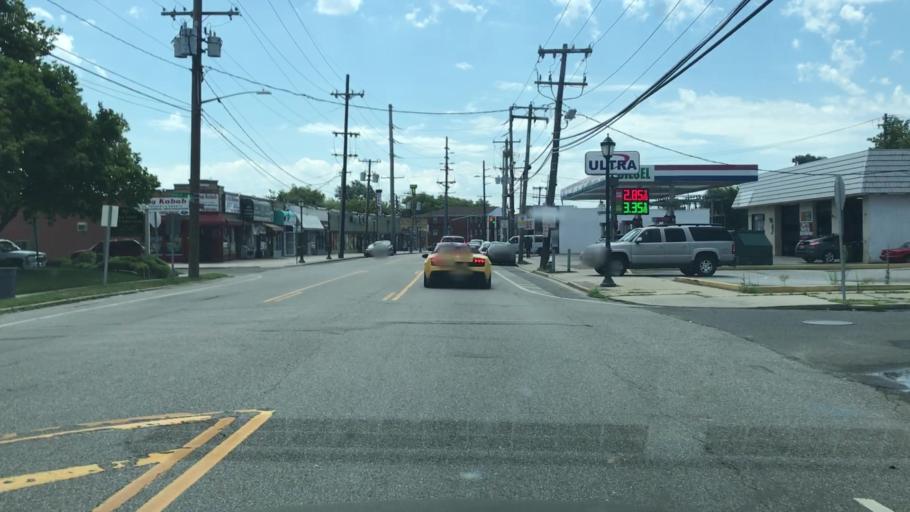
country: US
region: New York
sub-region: Nassau County
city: North Valley Stream
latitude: 40.6782
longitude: -73.7101
